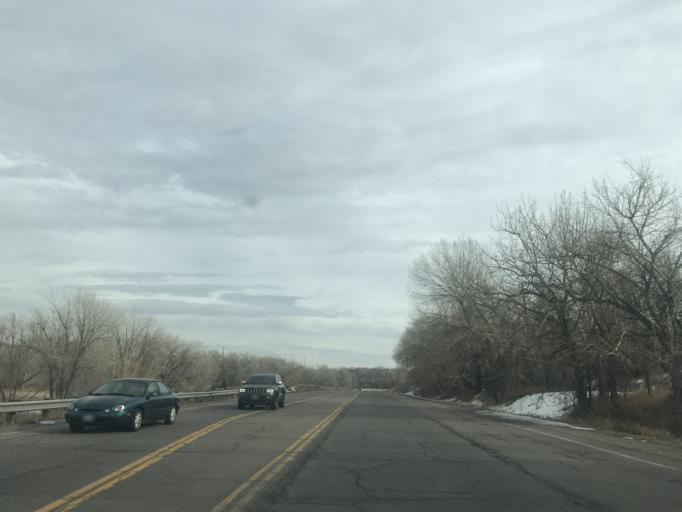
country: US
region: Colorado
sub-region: Douglas County
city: Highlands Ranch
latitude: 39.5648
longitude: -105.0080
